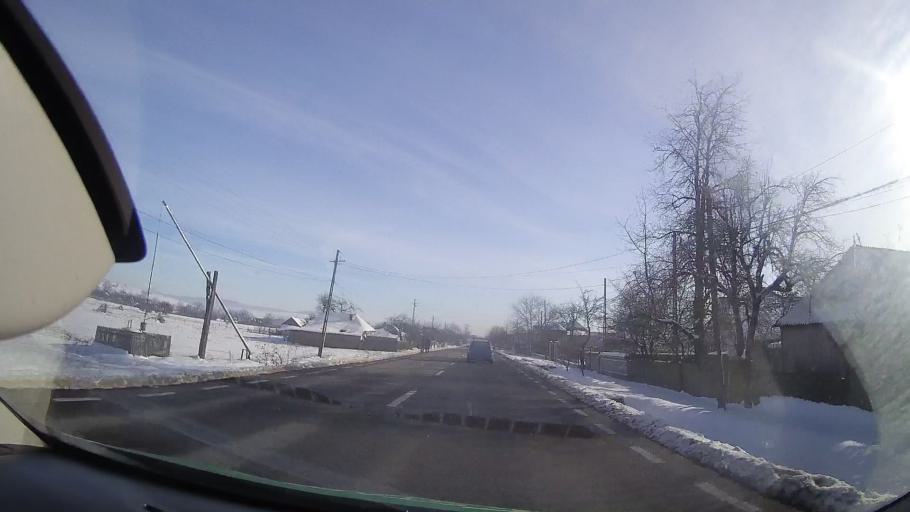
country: RO
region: Neamt
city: Bodesti
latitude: 47.0547
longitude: 26.3966
